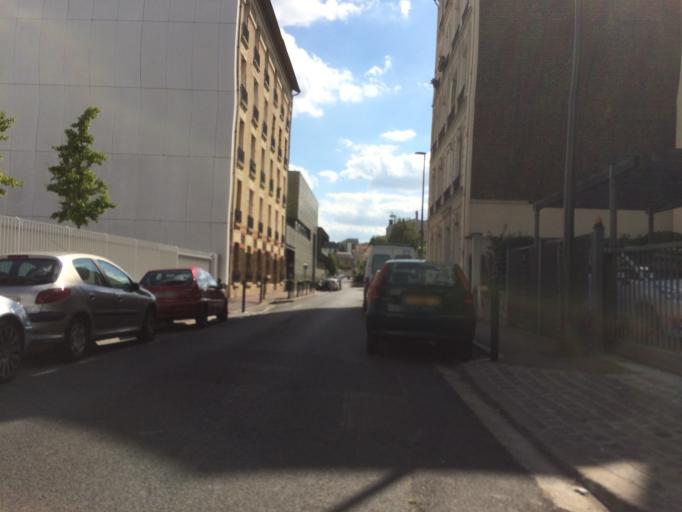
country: FR
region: Ile-de-France
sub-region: Departement des Hauts-de-Seine
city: Suresnes
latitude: 48.8745
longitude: 2.2261
